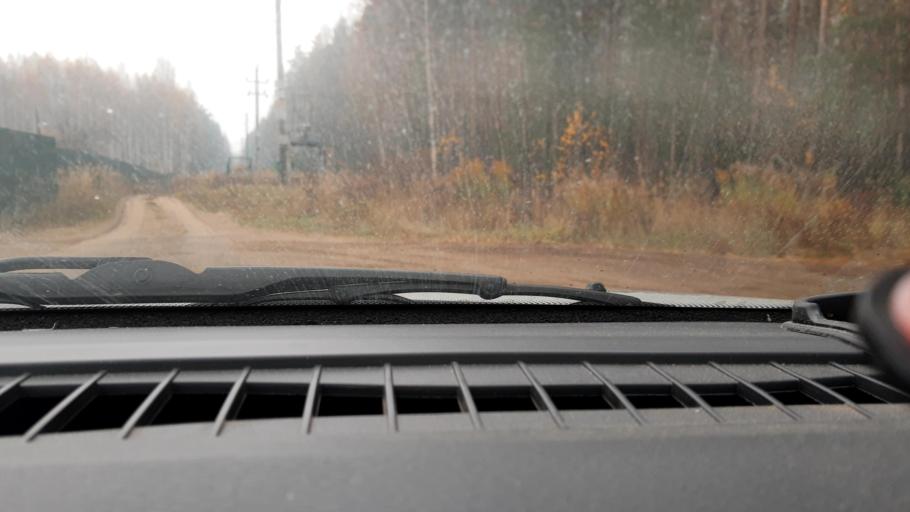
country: RU
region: Nizjnij Novgorod
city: Sitniki
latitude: 56.4256
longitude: 44.0550
